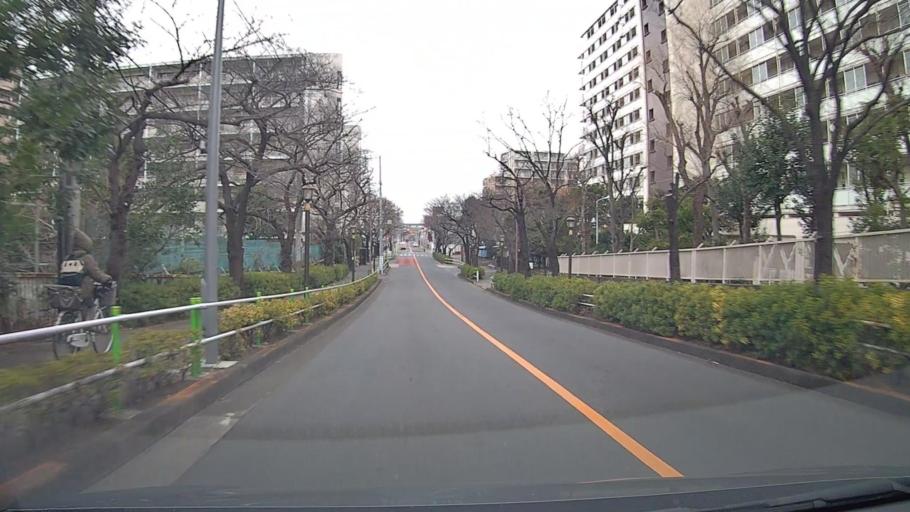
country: JP
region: Saitama
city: Shimotoda
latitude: 35.7936
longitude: 139.6639
